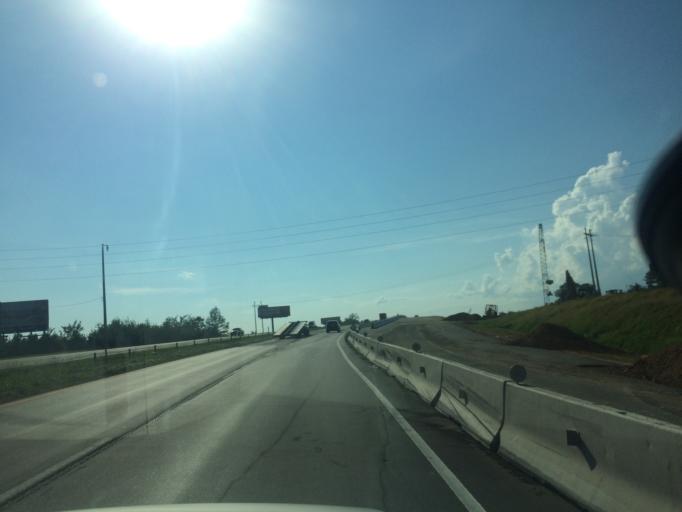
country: US
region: South Carolina
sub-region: Cherokee County
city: Blacksburg
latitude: 35.1593
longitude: -81.4634
